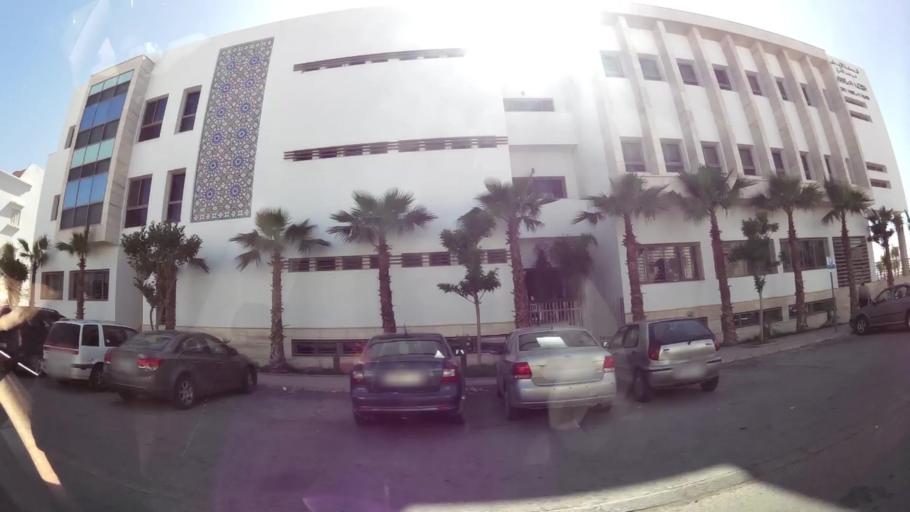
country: MA
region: Souss-Massa-Draa
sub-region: Agadir-Ida-ou-Tnan
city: Agadir
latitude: 30.4173
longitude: -9.5901
